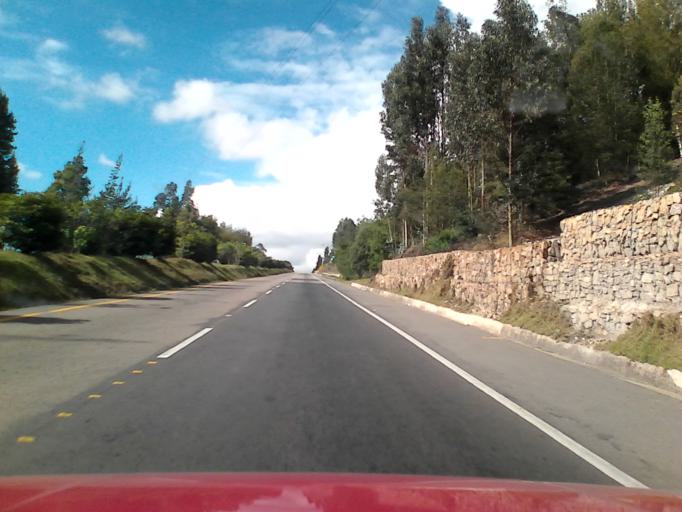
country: CO
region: Boyaca
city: Combita
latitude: 5.6387
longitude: -73.2901
